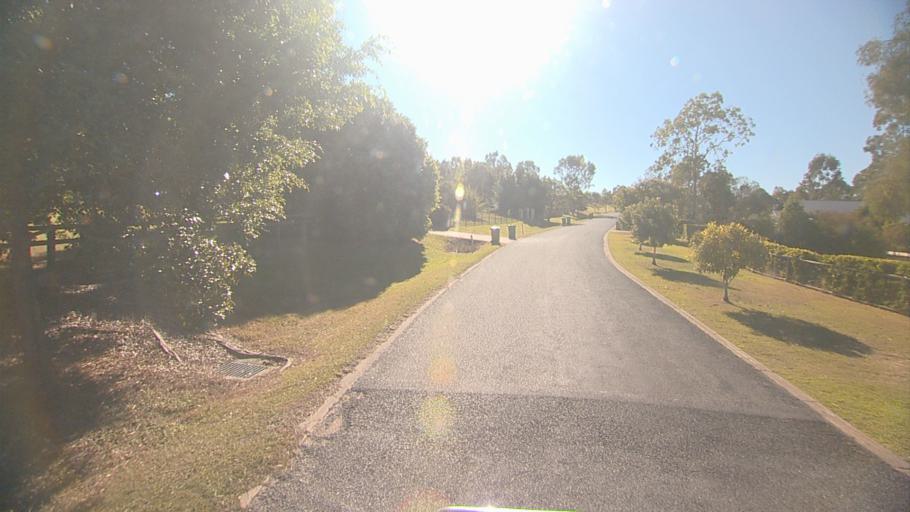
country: AU
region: Queensland
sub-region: Logan
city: North Maclean
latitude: -27.7438
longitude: 152.9583
